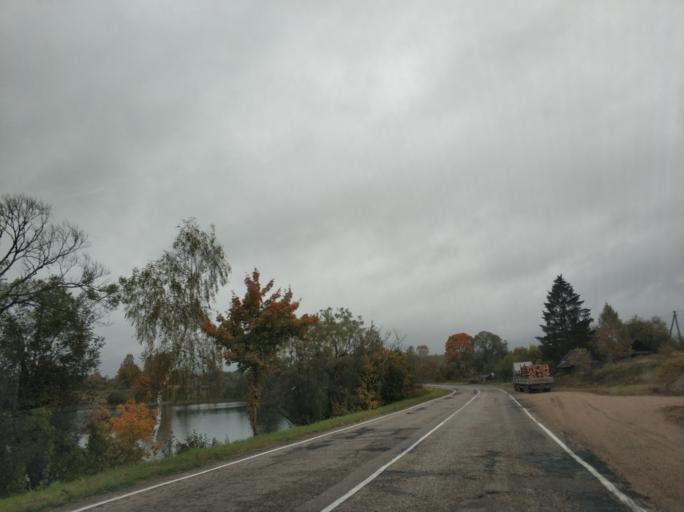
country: RU
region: Pskov
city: Sebezh
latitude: 56.2900
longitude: 28.5845
